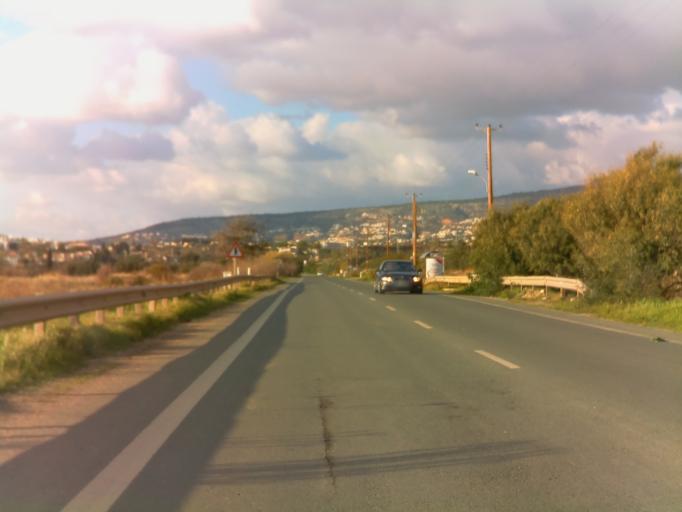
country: CY
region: Pafos
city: Kissonerga
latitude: 34.8435
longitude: 32.3871
